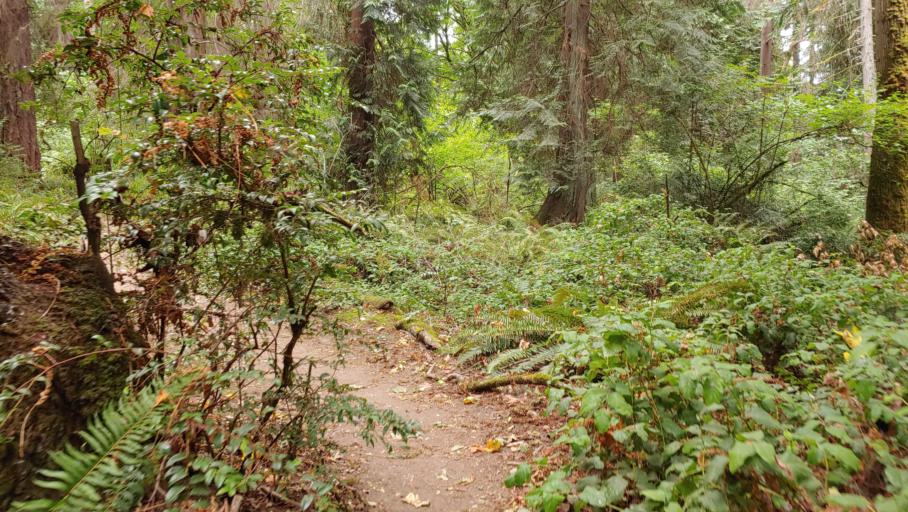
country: US
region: Washington
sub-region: King County
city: Mercer Island
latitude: 47.5591
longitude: -122.2516
